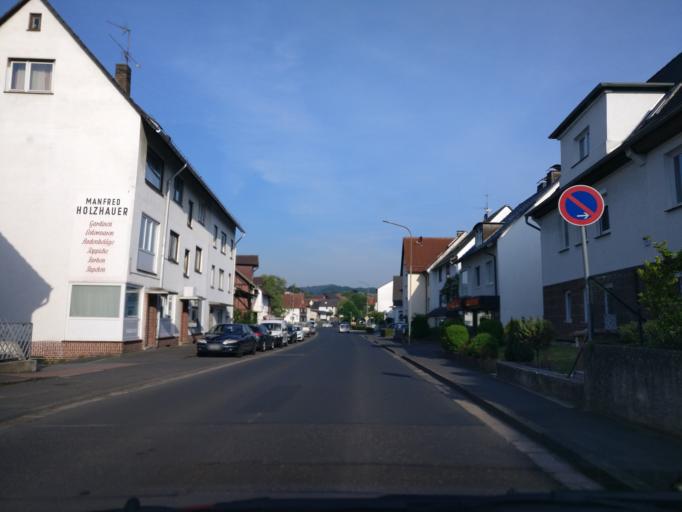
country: DE
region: Hesse
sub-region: Regierungsbezirk Kassel
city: Baunatal
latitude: 51.2731
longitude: 9.3805
